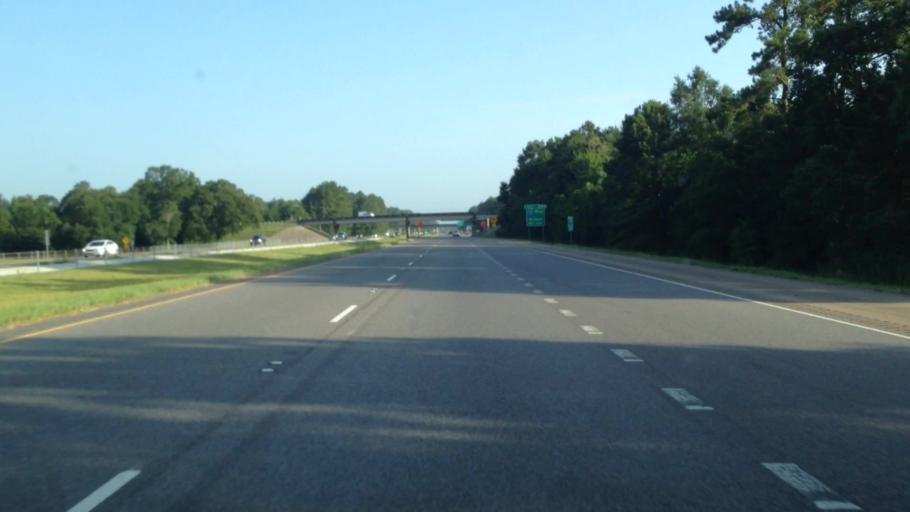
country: US
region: Louisiana
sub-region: Tangipahoa Parish
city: Hammond
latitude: 30.4733
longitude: -90.4849
